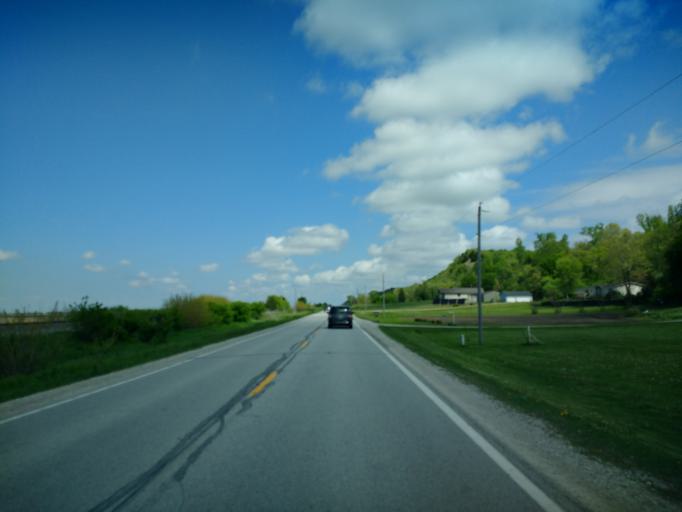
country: US
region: Iowa
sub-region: Harrison County
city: Missouri Valley
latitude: 41.4517
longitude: -95.8732
